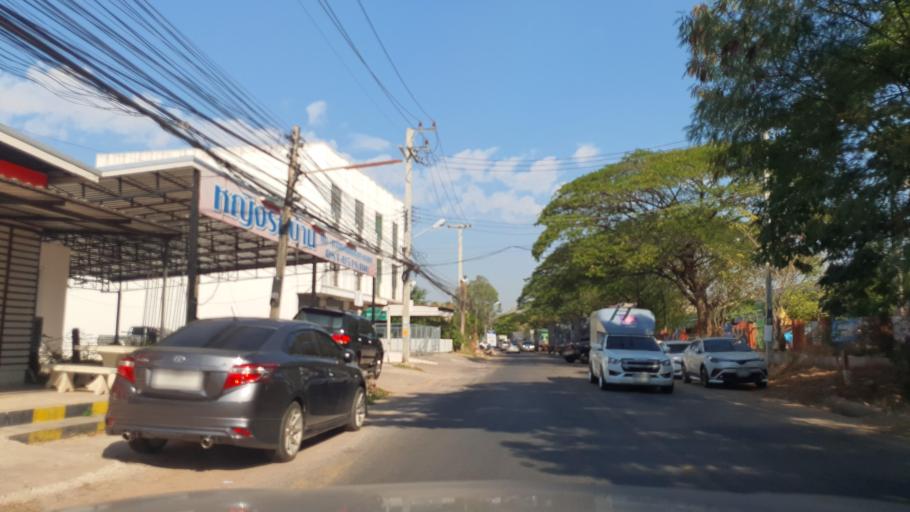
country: TH
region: Khon Kaen
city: Khon Kaen
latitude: 16.4346
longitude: 102.8146
